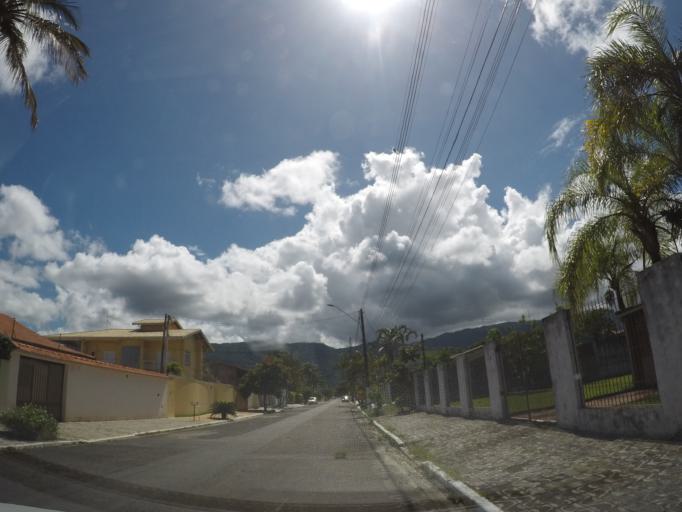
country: BR
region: Sao Paulo
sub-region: Mongagua
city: Mongagua
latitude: -24.0700
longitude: -46.5703
